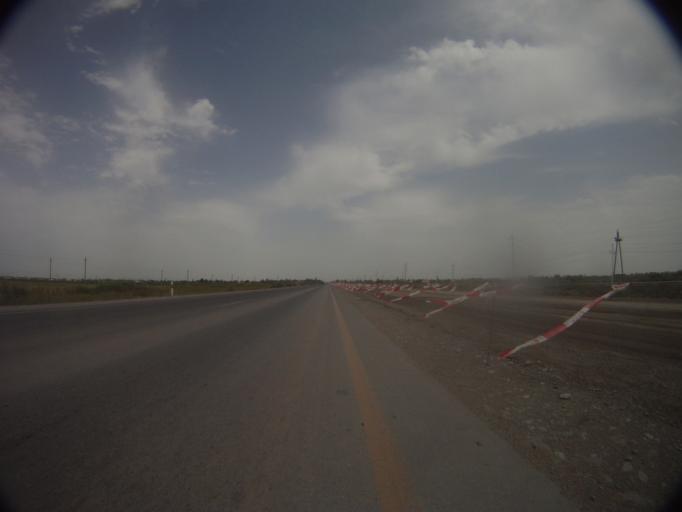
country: AZ
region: Ucar
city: Ujar
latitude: 40.4944
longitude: 47.6430
